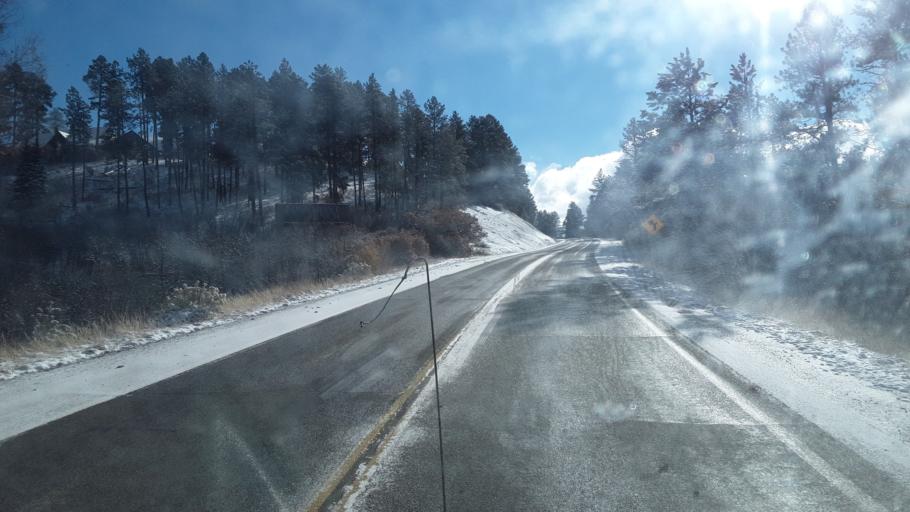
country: US
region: Colorado
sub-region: La Plata County
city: Durango
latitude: 37.3127
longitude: -107.8000
